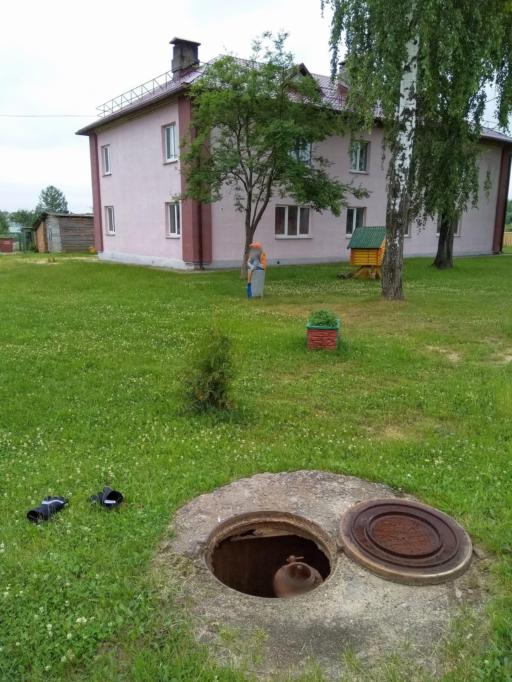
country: BY
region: Mogilev
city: Myazhysyatki
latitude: 53.7803
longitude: 30.0098
